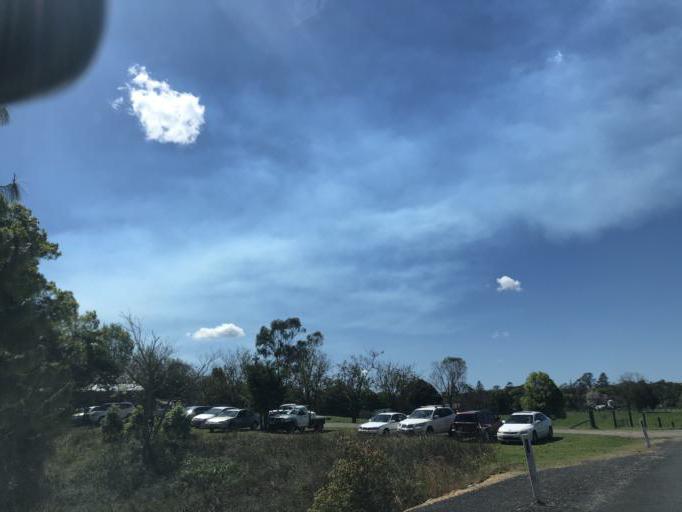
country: AU
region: New South Wales
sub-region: Bellingen
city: Bellingen
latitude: -30.4559
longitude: 152.9088
